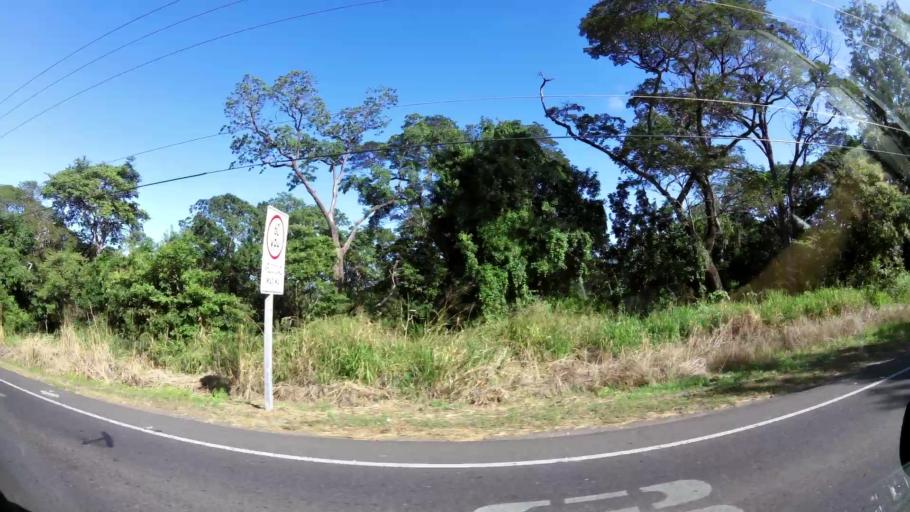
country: CR
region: Guanacaste
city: Sardinal
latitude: 10.5600
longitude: -85.5911
